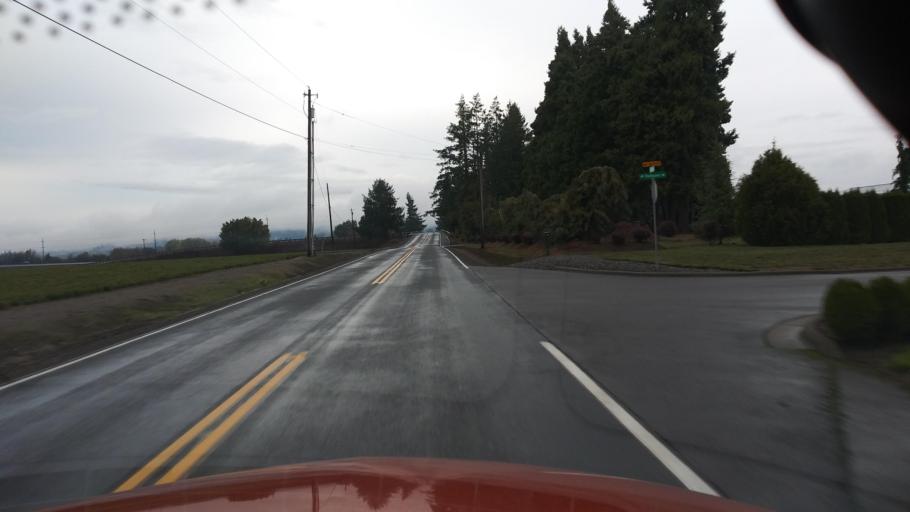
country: US
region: Oregon
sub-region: Washington County
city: North Plains
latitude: 45.5941
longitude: -123.0149
